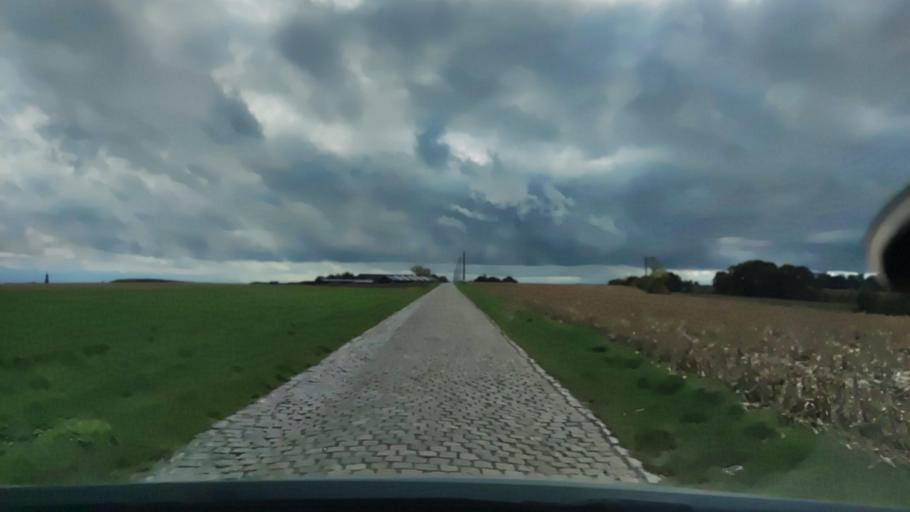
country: BE
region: Wallonia
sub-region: Province du Brabant Wallon
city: Jodoigne
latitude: 50.7349
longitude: 4.8627
